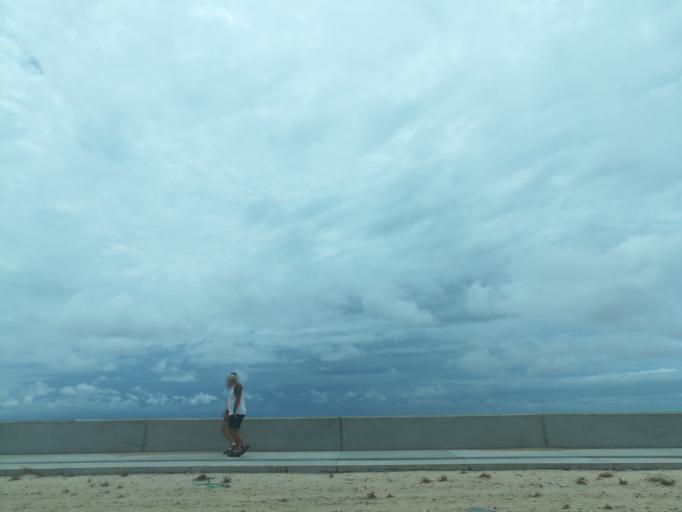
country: NG
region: Lagos
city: Lagos
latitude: 6.4022
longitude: 3.4120
